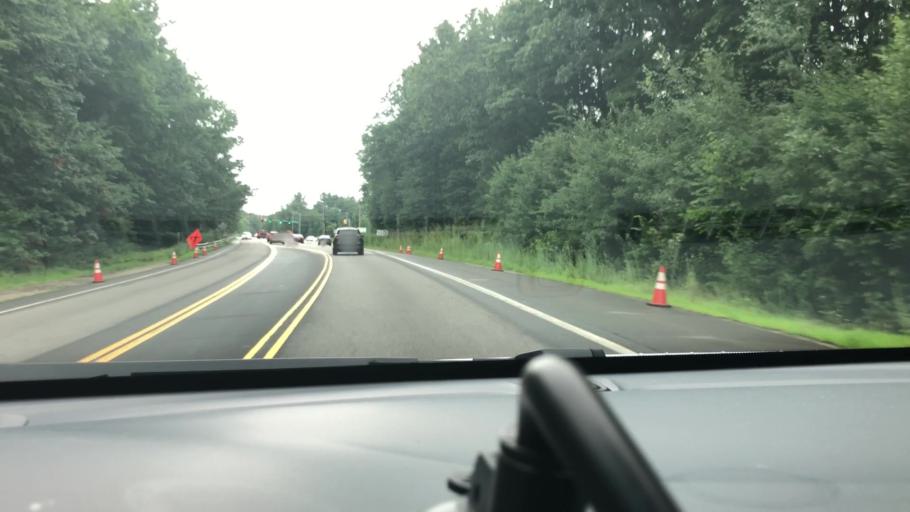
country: US
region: New Hampshire
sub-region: Hillsborough County
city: Bedford
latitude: 42.9671
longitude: -71.5064
